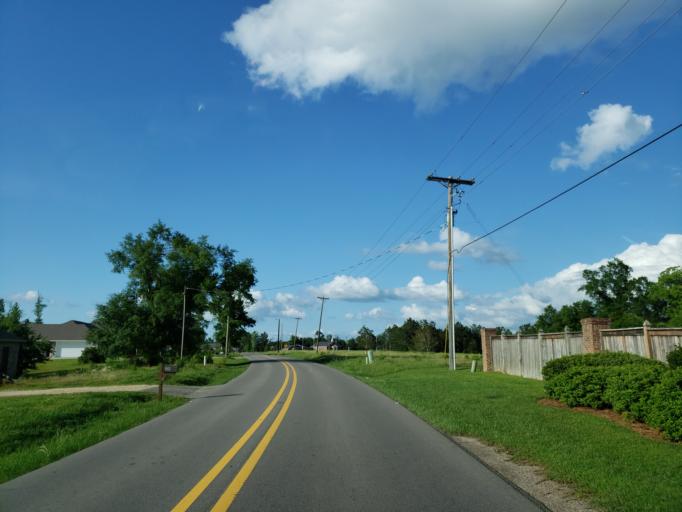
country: US
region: Mississippi
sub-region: Forrest County
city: Petal
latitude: 31.3465
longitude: -89.2316
